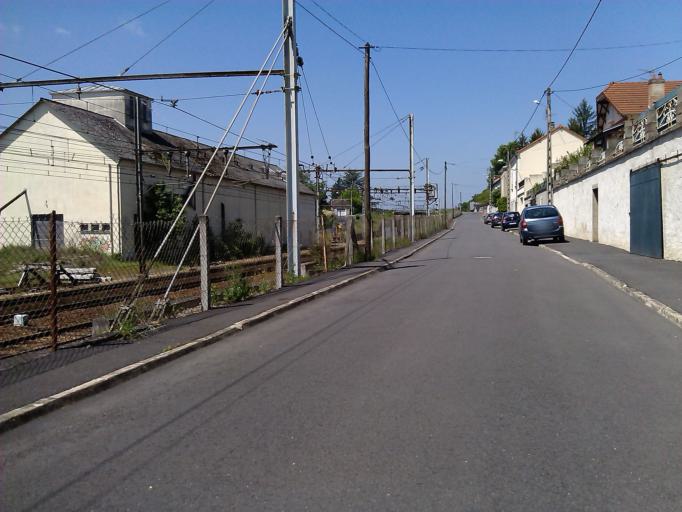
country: FR
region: Centre
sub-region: Departement de l'Indre
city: Saint-Marcel
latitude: 46.5963
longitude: 1.5135
